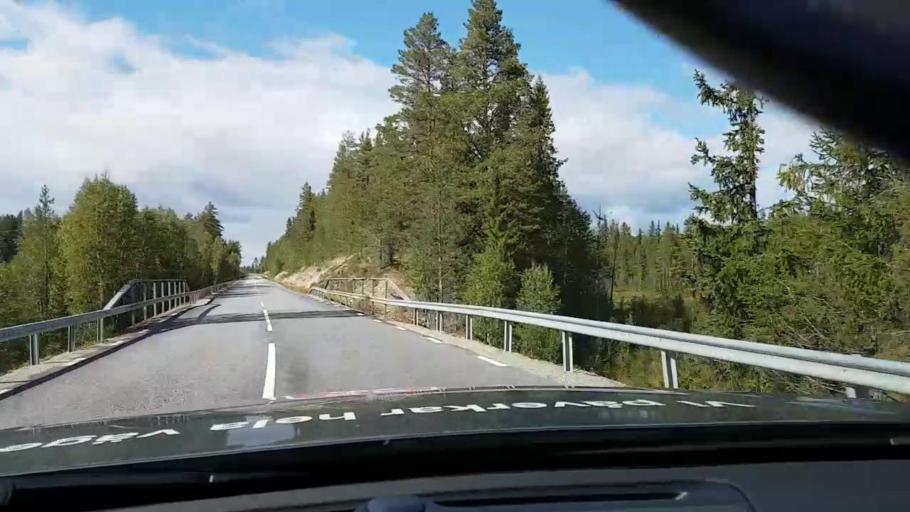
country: SE
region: Vaesterbotten
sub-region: Asele Kommun
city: Asele
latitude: 63.8383
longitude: 17.4340
